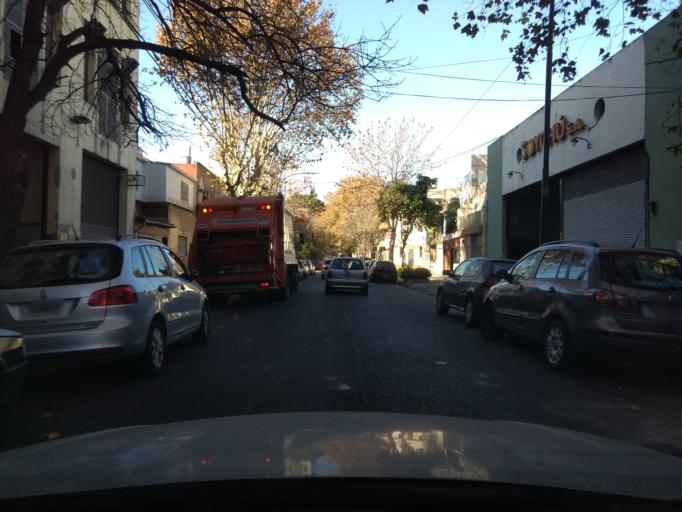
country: AR
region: Buenos Aires F.D.
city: Villa Santa Rita
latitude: -34.6196
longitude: -58.4767
